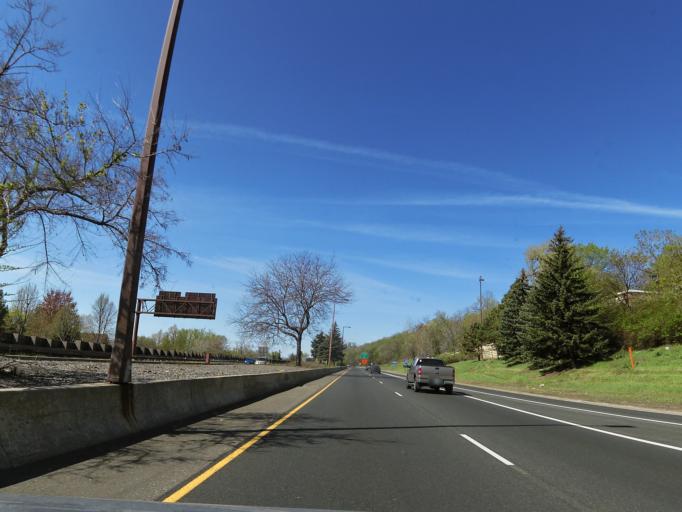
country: US
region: Minnesota
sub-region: Ramsey County
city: Saint Paul
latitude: 44.9398
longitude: -93.1163
